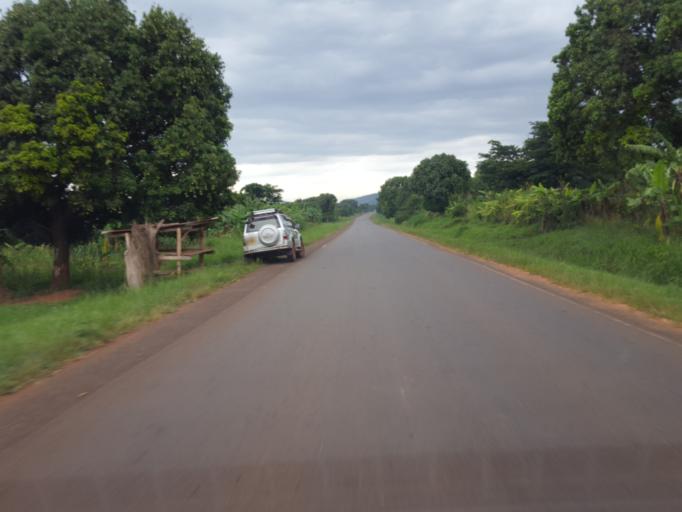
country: UG
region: Central Region
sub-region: Kiboga District
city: Kiboga
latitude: 0.8605
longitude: 31.8627
